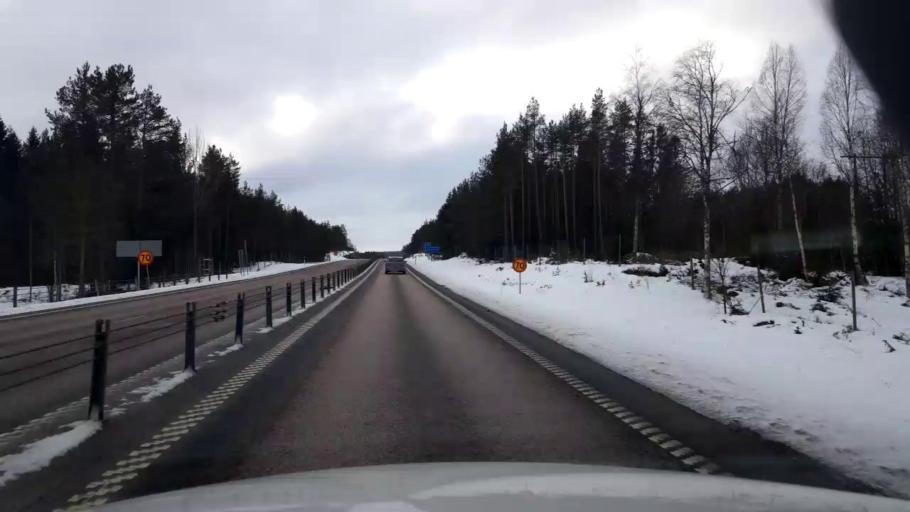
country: SE
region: Gaevleborg
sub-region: Hudiksvalls Kommun
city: Hudiksvall
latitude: 61.8076
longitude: 17.1826
